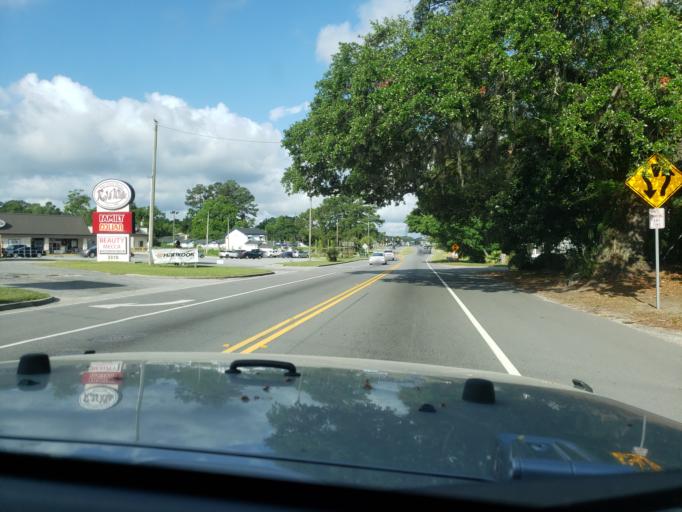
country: US
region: Georgia
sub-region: Chatham County
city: Savannah
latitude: 32.0554
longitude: -81.1359
